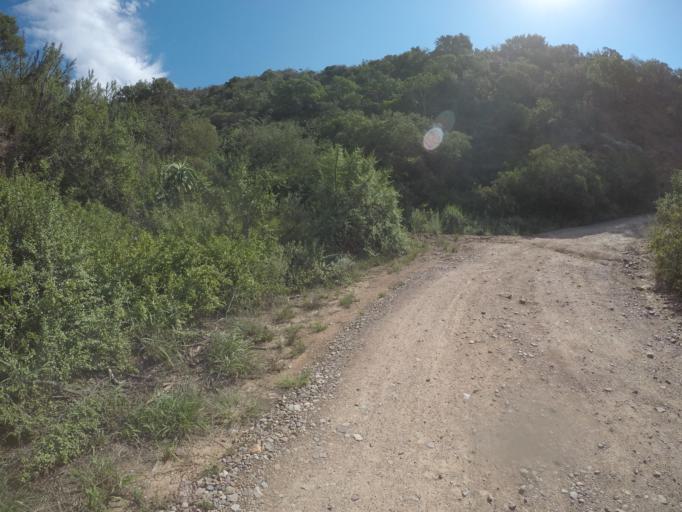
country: ZA
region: Eastern Cape
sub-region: Cacadu District Municipality
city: Kareedouw
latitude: -33.6567
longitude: 24.4258
